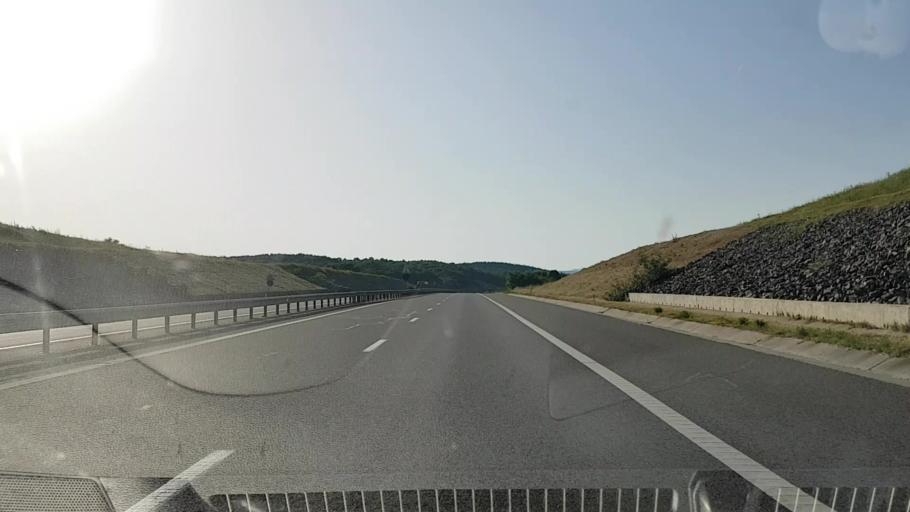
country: RO
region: Cluj
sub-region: Comuna Savadisla
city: Savadisla
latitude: 46.6615
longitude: 23.4963
